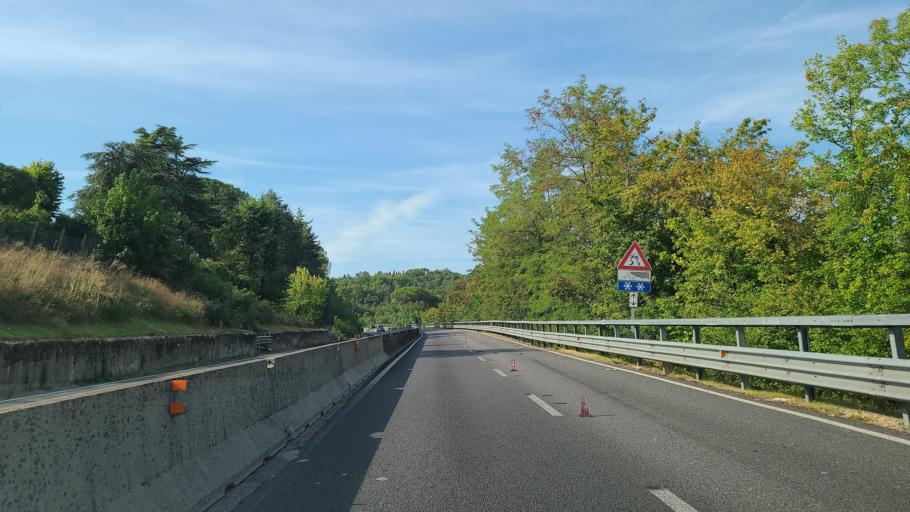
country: IT
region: Tuscany
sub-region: Province of Florence
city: San Casciano in Val di Pesa
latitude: 43.6786
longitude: 11.2108
